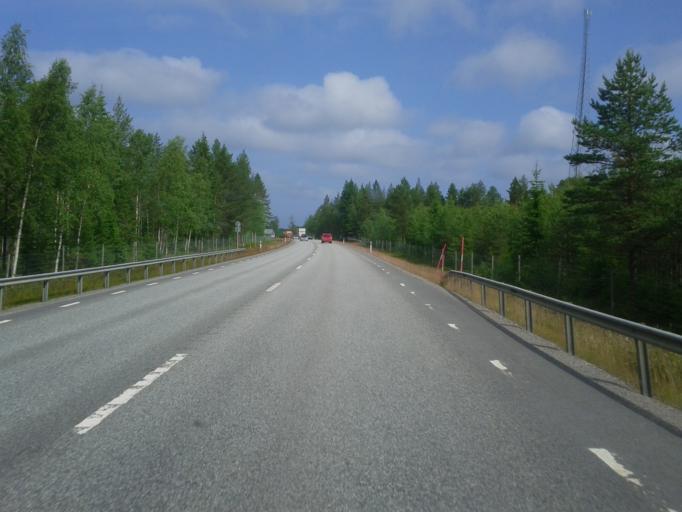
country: SE
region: Vaesterbotten
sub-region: Skelleftea Kommun
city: Burea
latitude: 64.4663
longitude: 21.2929
